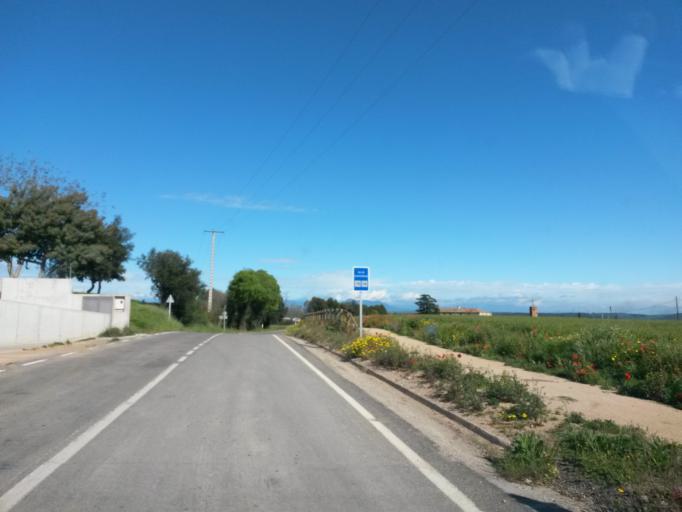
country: ES
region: Catalonia
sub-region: Provincia de Girona
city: Juia
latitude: 42.0189
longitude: 2.9066
